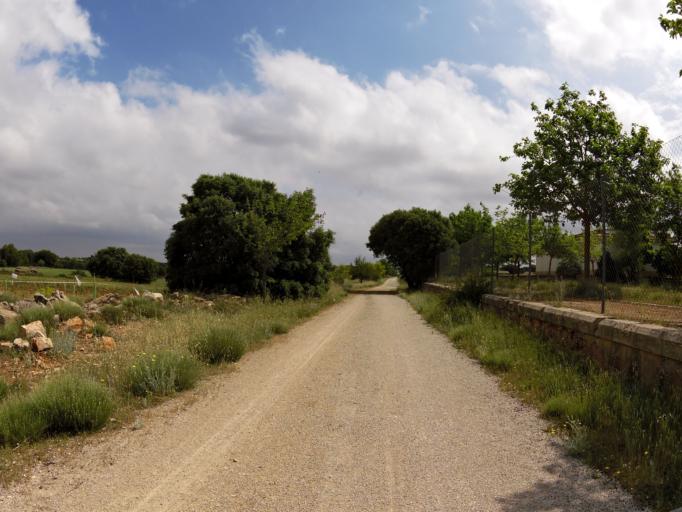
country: ES
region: Castille-La Mancha
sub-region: Provincia de Albacete
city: Robledo
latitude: 38.7698
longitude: -2.4482
